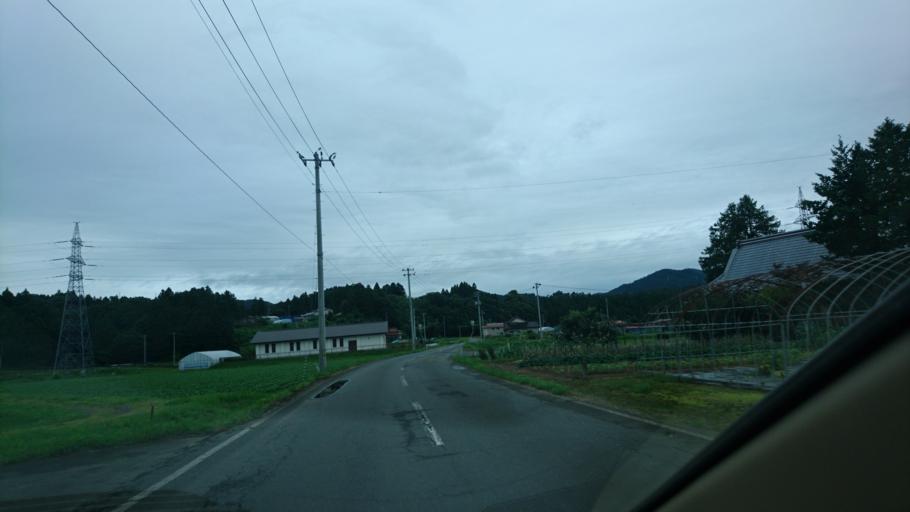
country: JP
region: Iwate
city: Mizusawa
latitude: 39.0715
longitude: 141.1823
